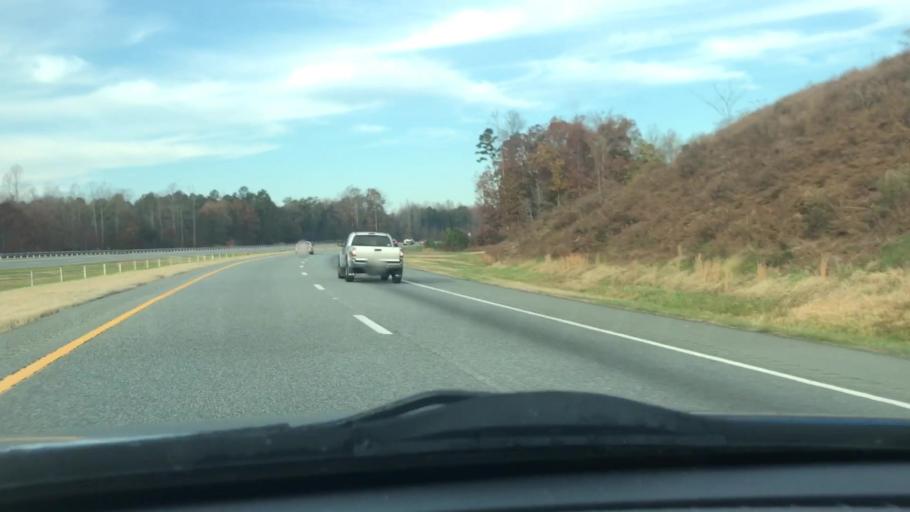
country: US
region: North Carolina
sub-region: Randolph County
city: Archdale
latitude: 35.9363
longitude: -79.9551
